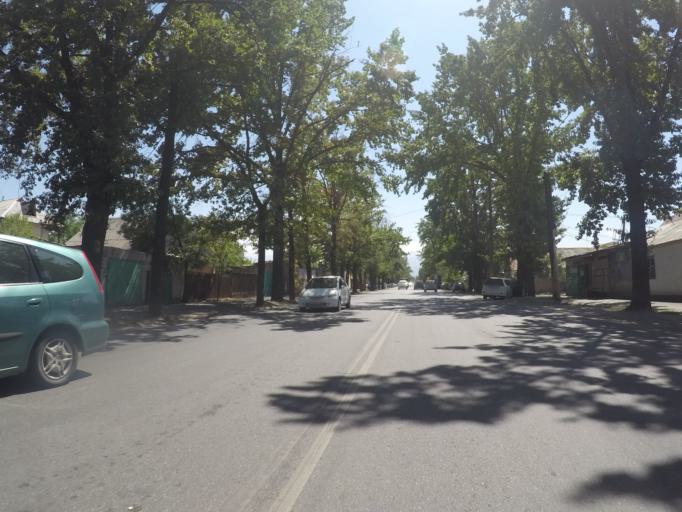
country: KG
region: Chuy
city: Bishkek
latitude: 42.8514
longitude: 74.5770
